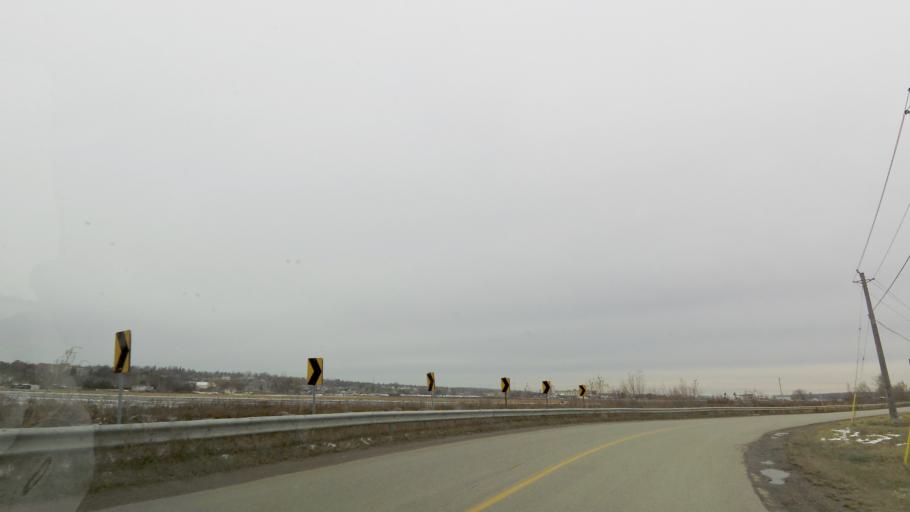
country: CA
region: Ontario
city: Bradford West Gwillimbury
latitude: 44.1059
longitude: -79.5562
